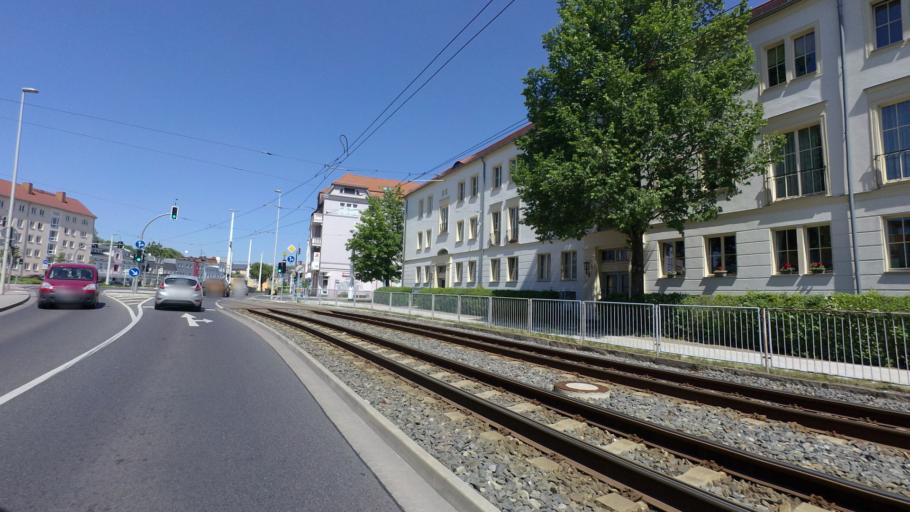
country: DE
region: Brandenburg
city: Cottbus
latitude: 51.7441
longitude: 14.3321
